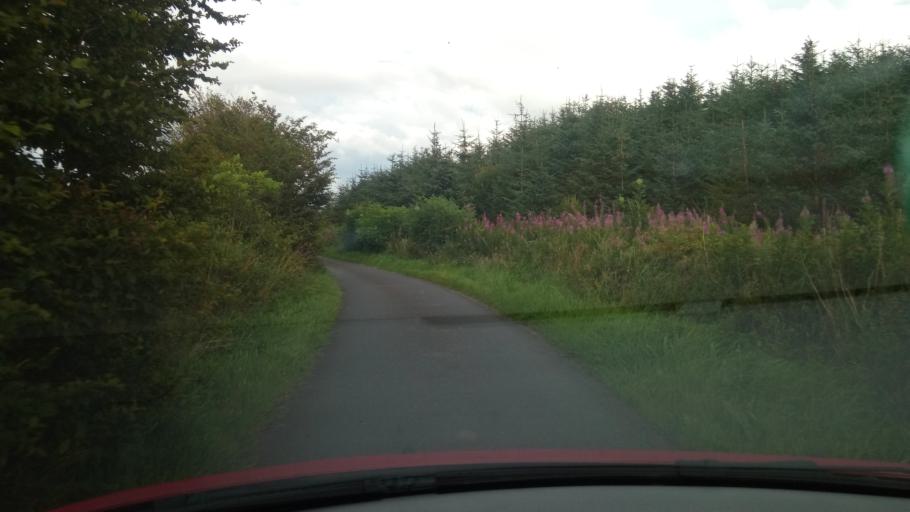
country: GB
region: Scotland
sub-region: The Scottish Borders
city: Hawick
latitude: 55.4165
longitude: -2.7642
